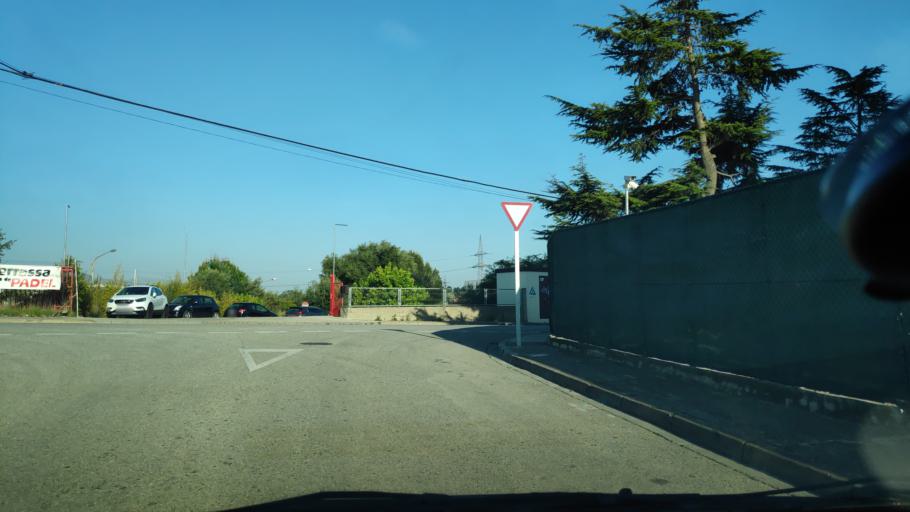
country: ES
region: Catalonia
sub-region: Provincia de Barcelona
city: Terrassa
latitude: 41.5439
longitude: 2.0364
